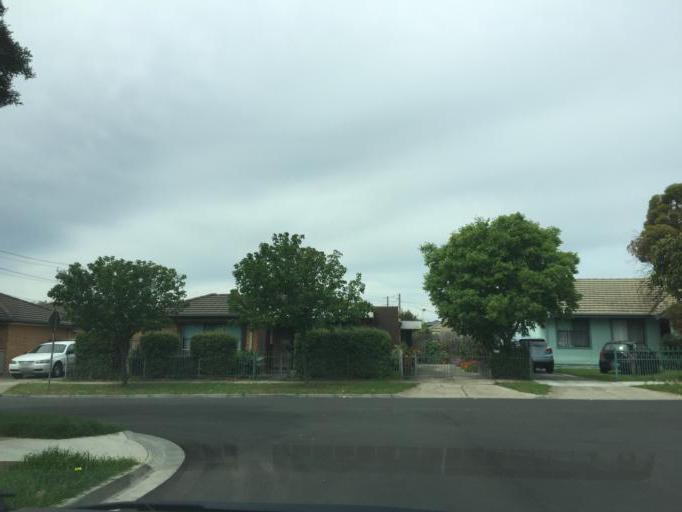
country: AU
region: Victoria
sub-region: Maribyrnong
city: Maidstone
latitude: -37.7824
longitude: 144.8732
